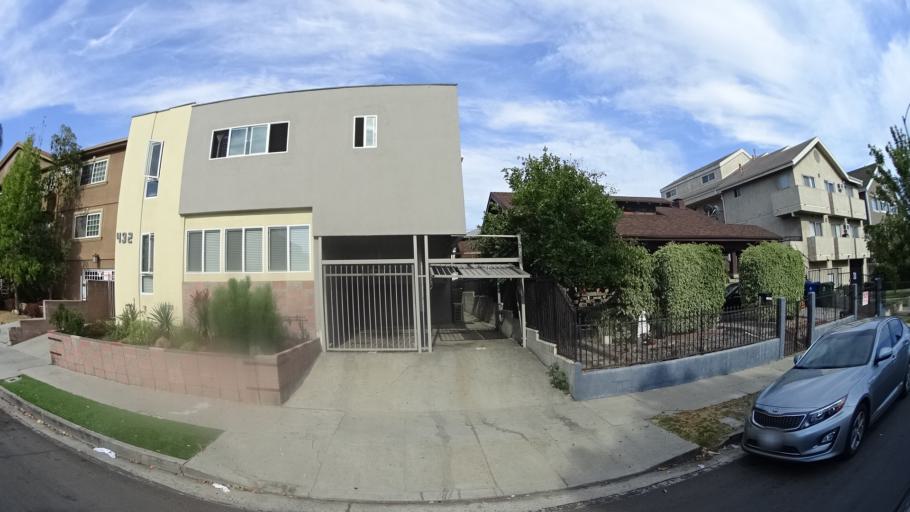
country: US
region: California
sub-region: Los Angeles County
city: Hollywood
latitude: 34.0785
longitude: -118.3080
